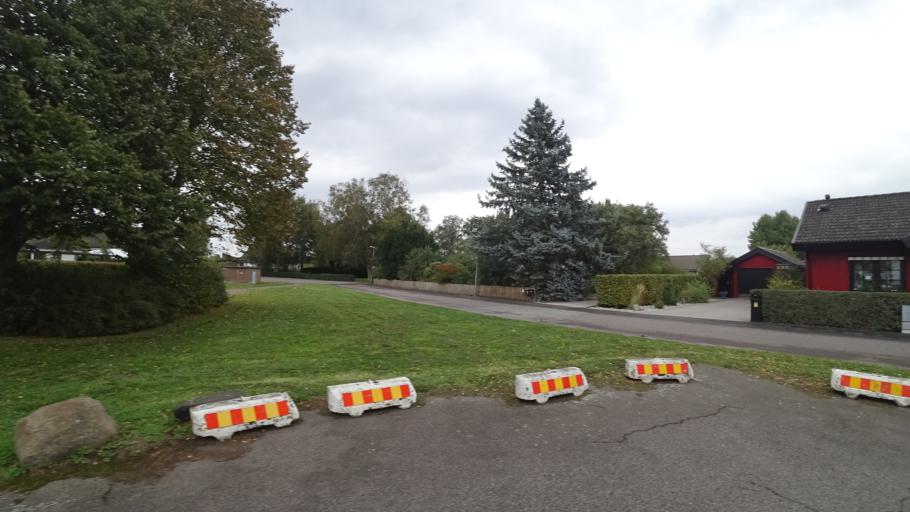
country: SE
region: Skane
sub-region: Kavlinge Kommun
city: Kaevlinge
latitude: 55.8045
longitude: 13.1145
